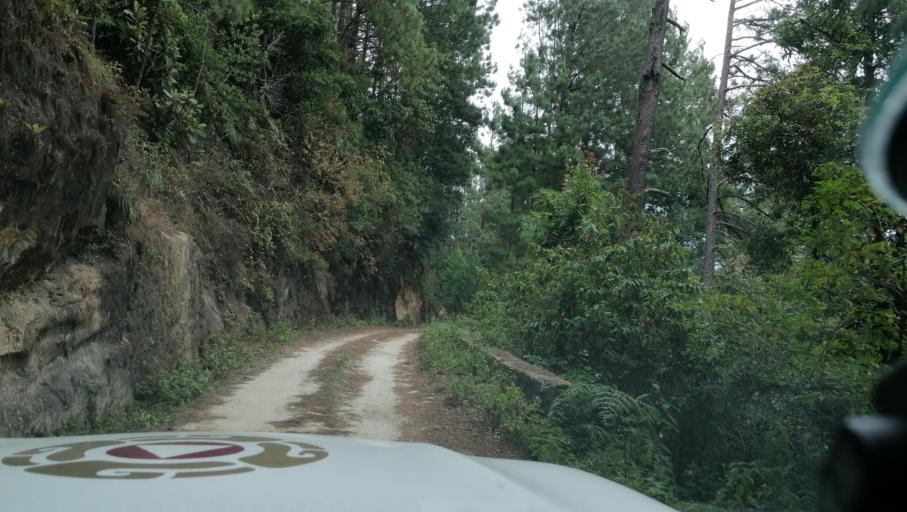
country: MX
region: Chiapas
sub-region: Tapachula
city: Canton Villaflor
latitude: 15.2017
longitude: -92.2326
